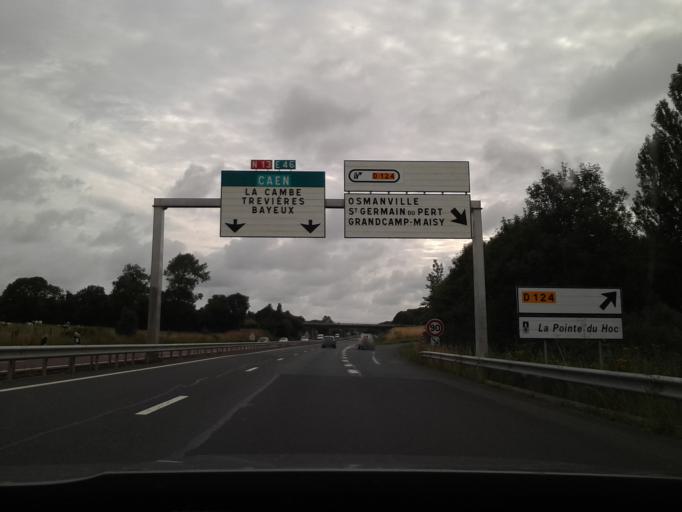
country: FR
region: Lower Normandy
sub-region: Departement du Calvados
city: Isigny-sur-Mer
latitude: 49.3295
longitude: -1.0751
